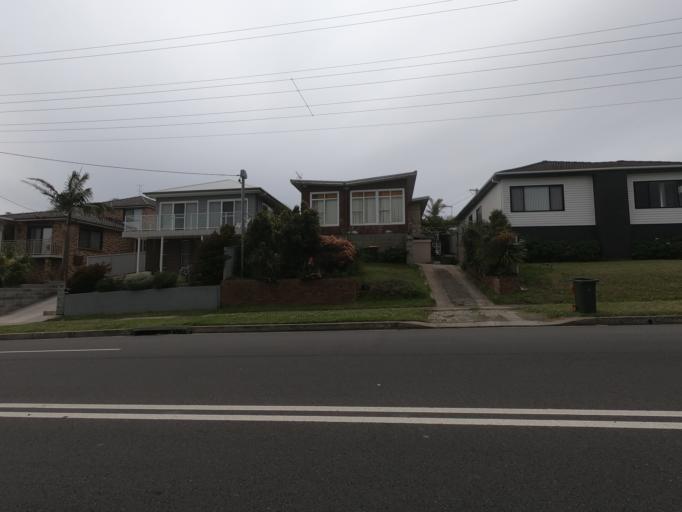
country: AU
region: New South Wales
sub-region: Wollongong
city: Port Kembla
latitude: -34.4871
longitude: 150.8994
